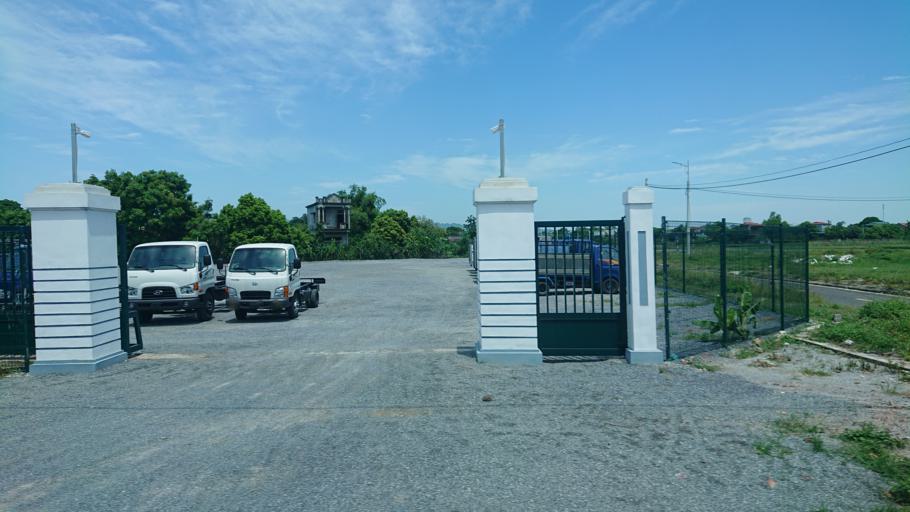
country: VN
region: Ha Nam
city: Thanh Pho Phu Ly
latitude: 20.5241
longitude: 105.9456
